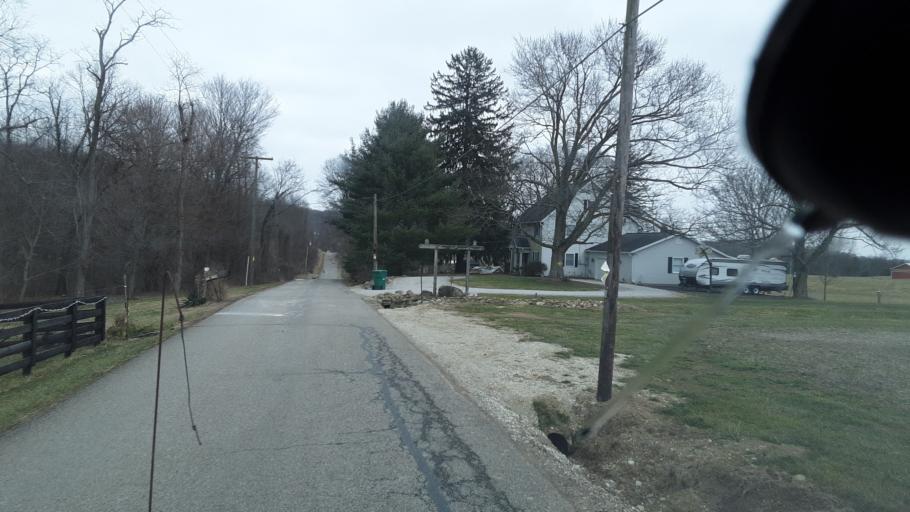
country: US
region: Ohio
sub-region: Perry County
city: Thornport
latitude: 39.9364
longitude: -82.4006
